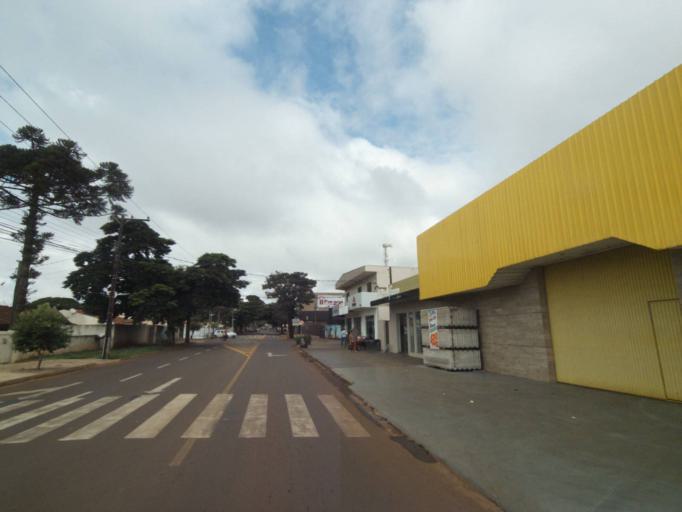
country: BR
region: Parana
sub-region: Campo Mourao
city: Campo Mourao
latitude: -24.0270
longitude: -52.3631
